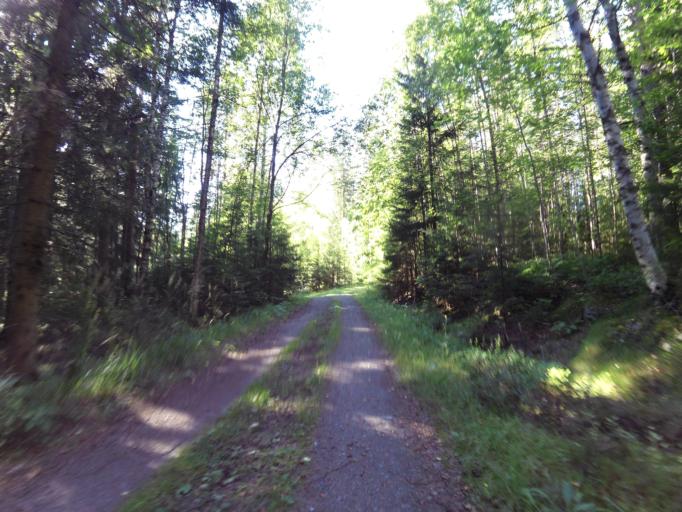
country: SE
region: Gaevleborg
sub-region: Hofors Kommun
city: Hofors
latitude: 60.5820
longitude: 16.4039
